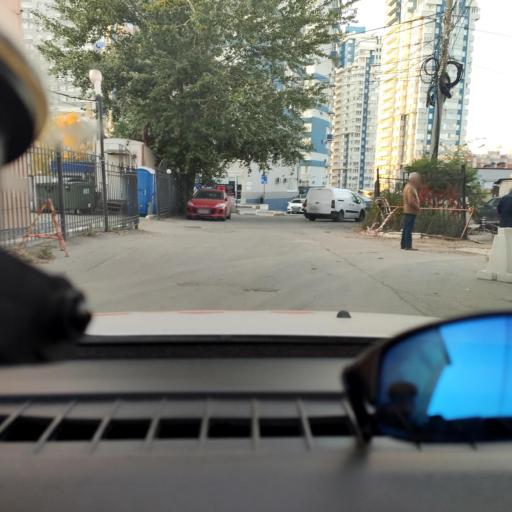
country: RU
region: Samara
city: Samara
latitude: 53.2202
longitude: 50.1546
